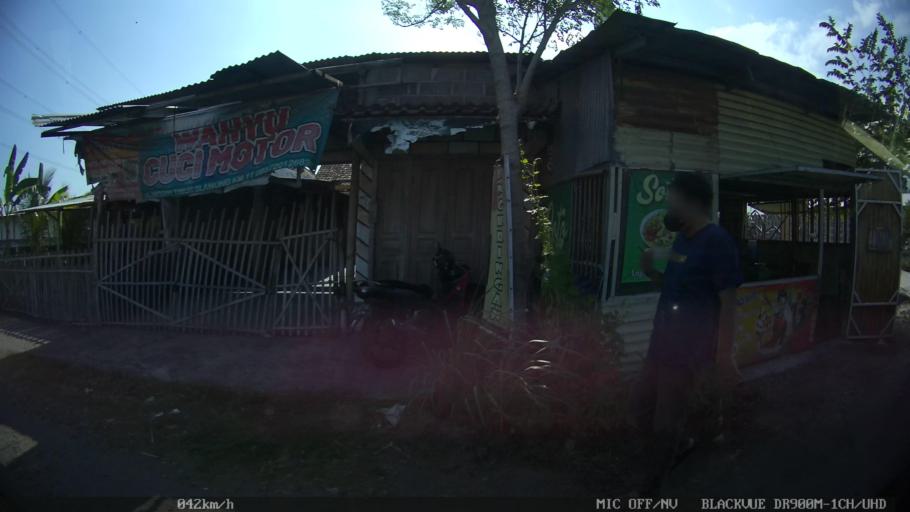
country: ID
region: Daerah Istimewa Yogyakarta
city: Sewon
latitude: -7.8838
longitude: 110.3887
